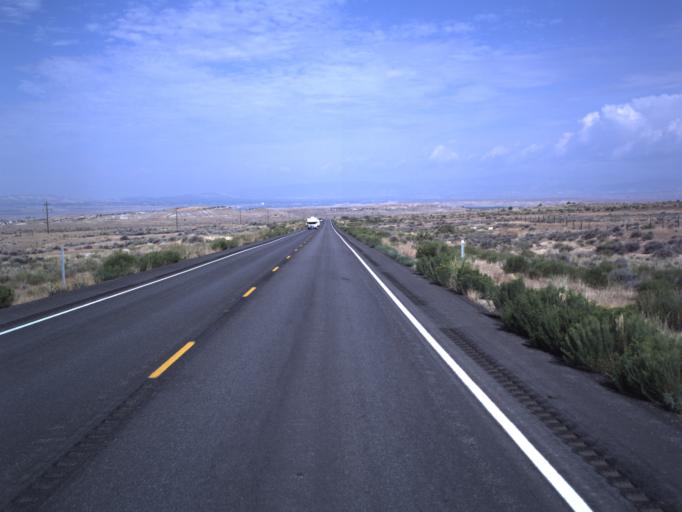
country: US
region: Utah
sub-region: Uintah County
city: Naples
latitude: 40.3288
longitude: -109.2753
